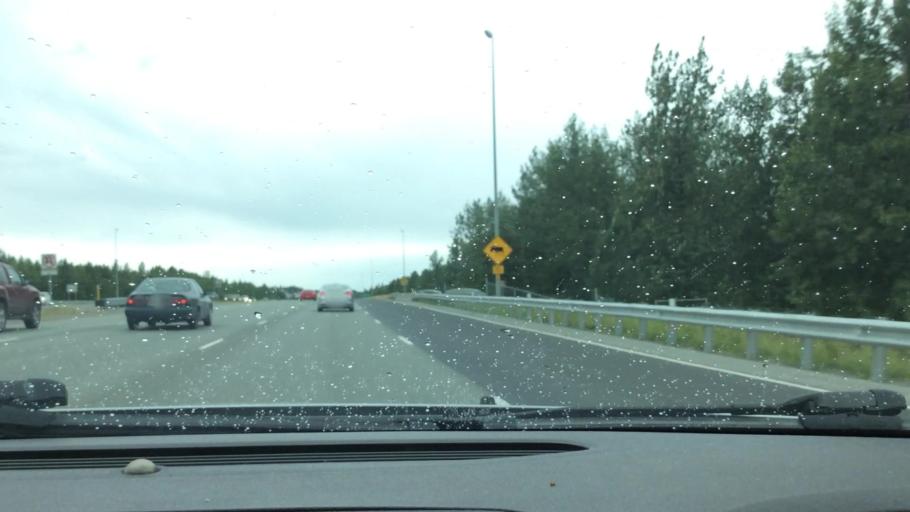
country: US
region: Alaska
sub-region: Anchorage Municipality
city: Elmendorf Air Force Base
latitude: 61.2389
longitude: -149.6929
